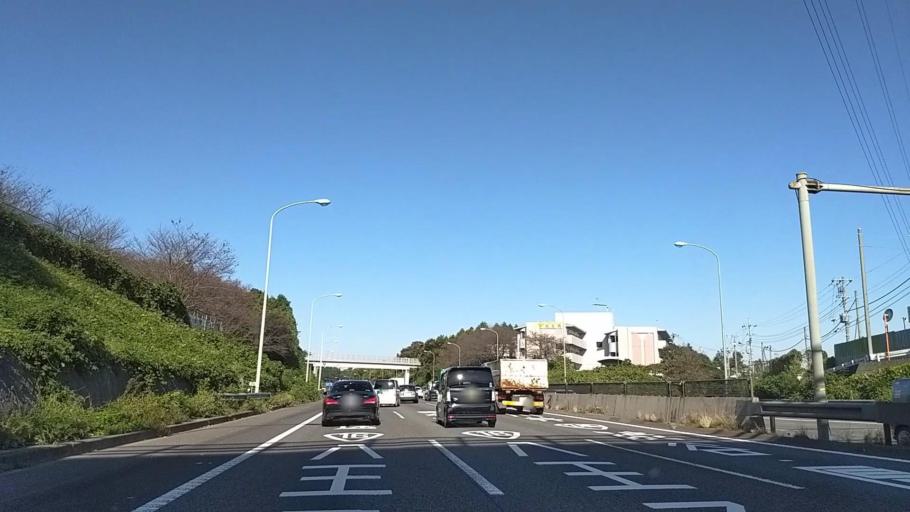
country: JP
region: Kanagawa
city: Minami-rinkan
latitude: 35.4900
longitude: 139.5054
